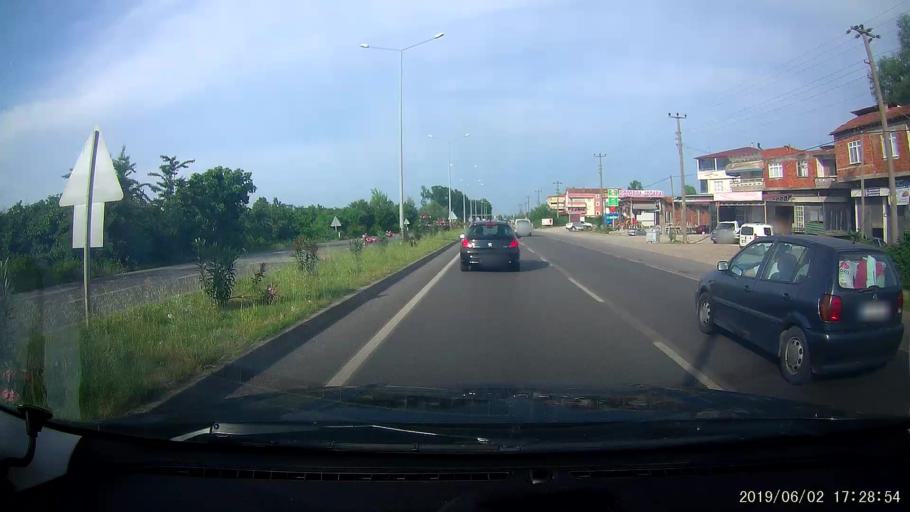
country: TR
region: Samsun
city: Carsamba
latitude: 41.2089
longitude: 36.7504
